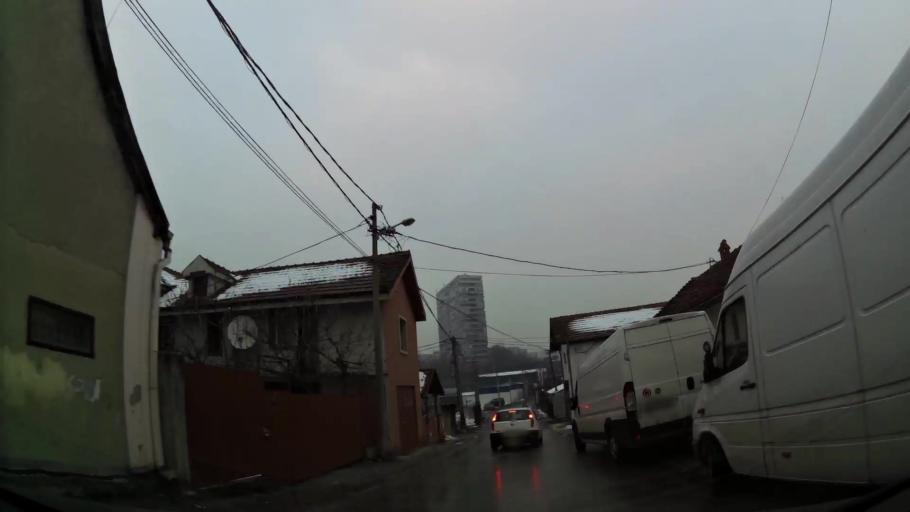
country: RS
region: Central Serbia
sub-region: Belgrade
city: Vozdovac
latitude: 44.7806
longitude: 20.4884
